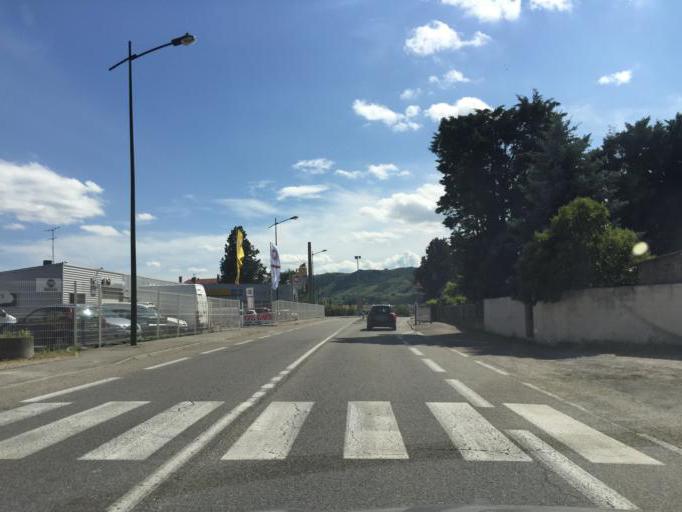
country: FR
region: Rhone-Alpes
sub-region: Departement de l'Ardeche
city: Tournon-sur-Rhone
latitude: 45.0563
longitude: 4.8395
